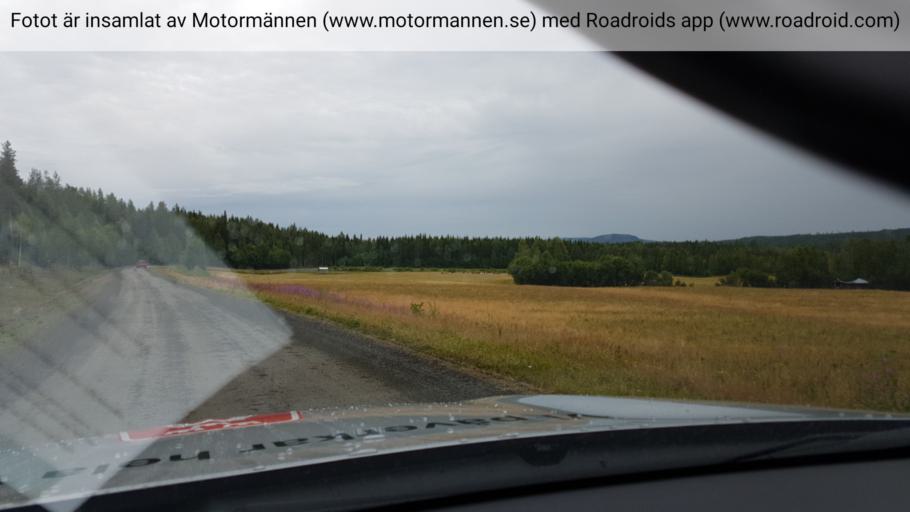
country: SE
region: Norrbotten
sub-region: Alvsbyns Kommun
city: AElvsbyn
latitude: 65.9460
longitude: 21.2322
